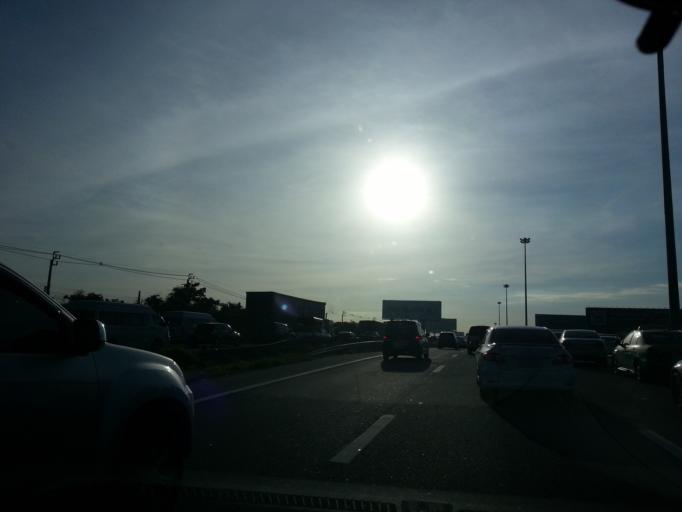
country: TH
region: Bangkok
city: Saphan Sung
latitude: 13.7322
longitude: 100.7078
